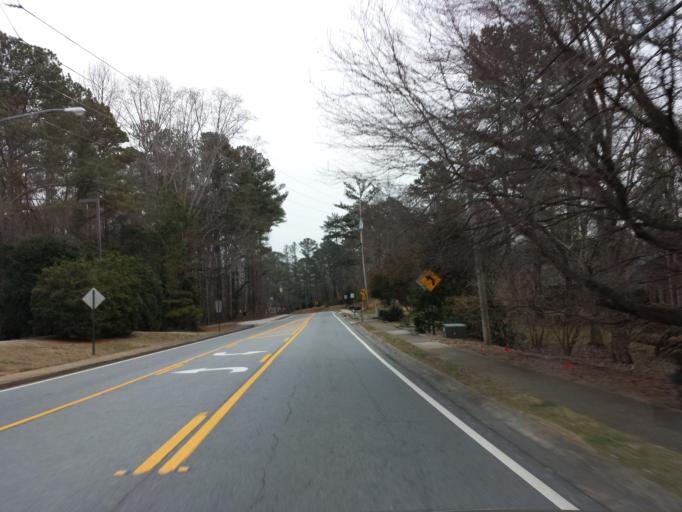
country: US
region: Georgia
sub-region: Fulton County
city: Roswell
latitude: 34.0163
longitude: -84.4204
